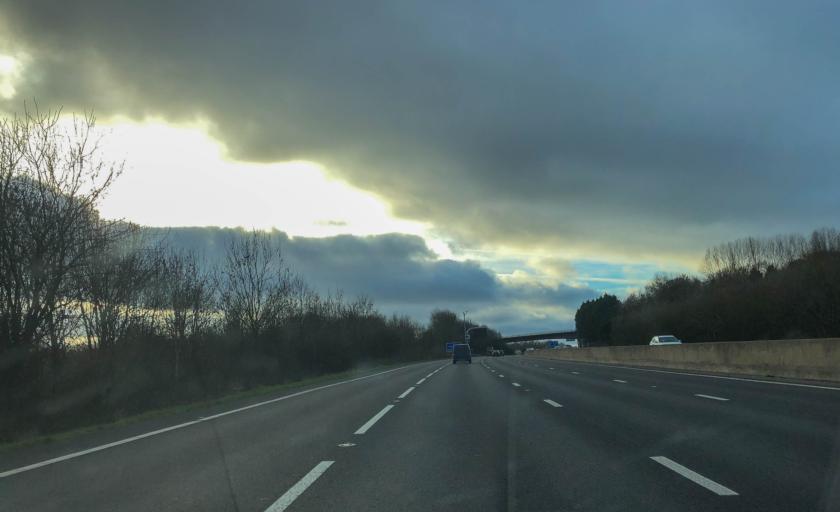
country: GB
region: England
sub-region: Surrey
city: Woldingham
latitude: 51.2604
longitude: -0.0348
